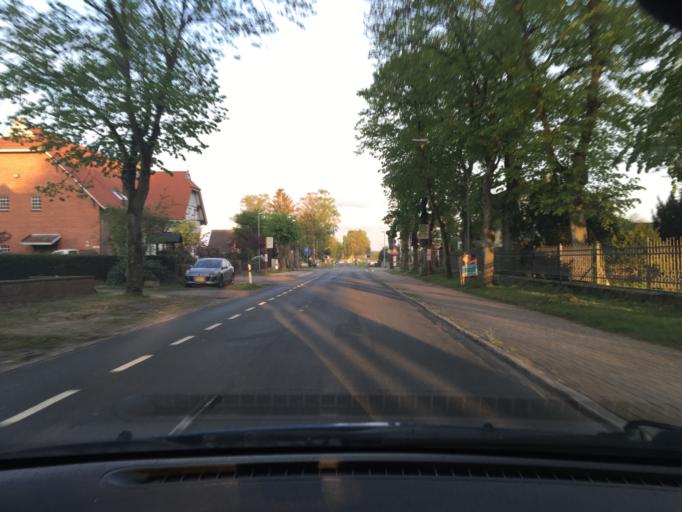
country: DE
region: Lower Saxony
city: Wulfsen
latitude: 53.3169
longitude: 10.1502
